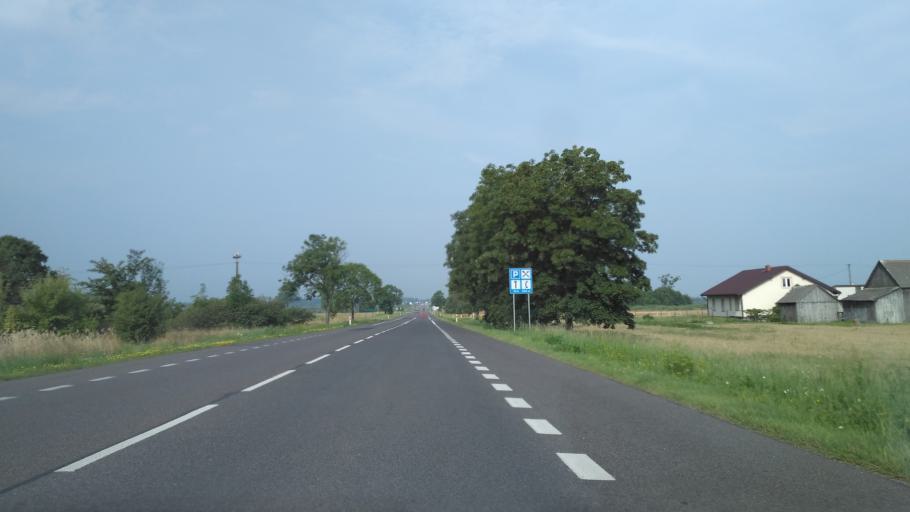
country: PL
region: Lublin Voivodeship
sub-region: Powiat swidnicki
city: Trawniki
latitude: 51.1659
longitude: 23.0610
